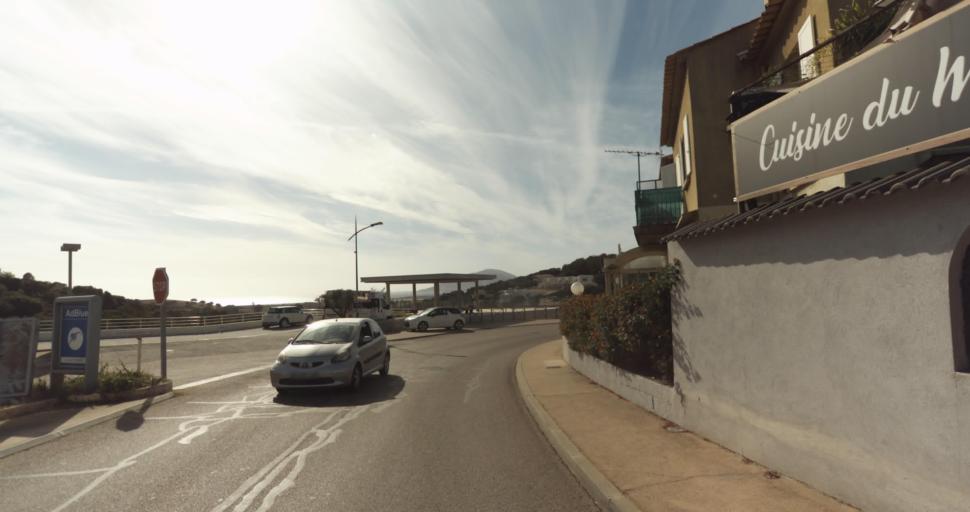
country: FR
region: Corsica
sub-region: Departement de la Corse-du-Sud
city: Afa
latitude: 41.9235
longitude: 8.8247
